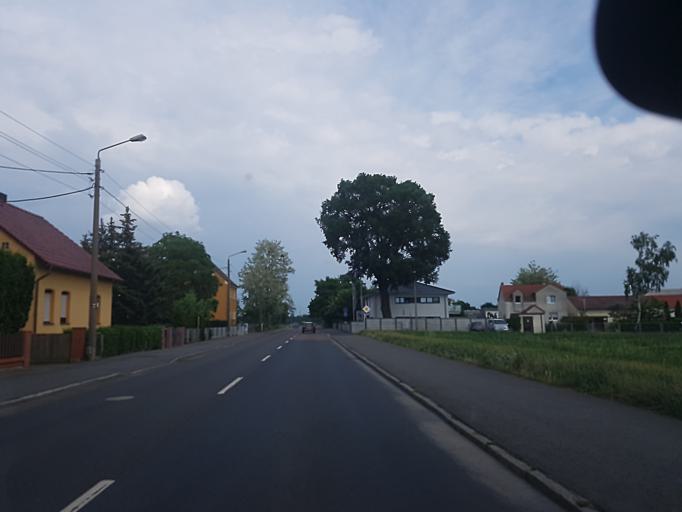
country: DE
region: Saxony-Anhalt
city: Wittenburg
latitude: 51.8756
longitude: 12.6105
